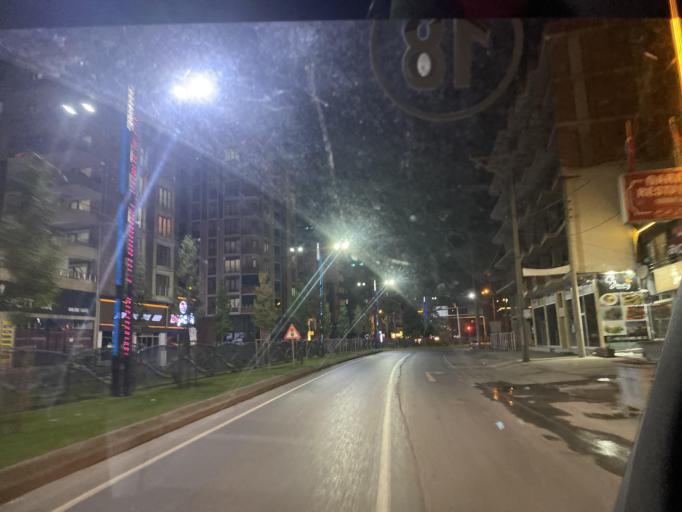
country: TR
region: Trabzon
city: Yomra
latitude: 40.9581
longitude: 39.8521
